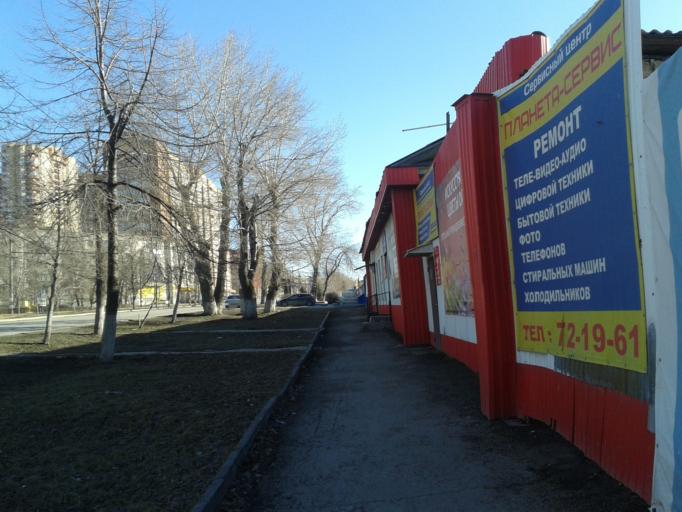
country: RU
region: Ulyanovsk
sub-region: Ulyanovskiy Rayon
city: Ulyanovsk
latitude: 54.2986
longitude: 48.3805
